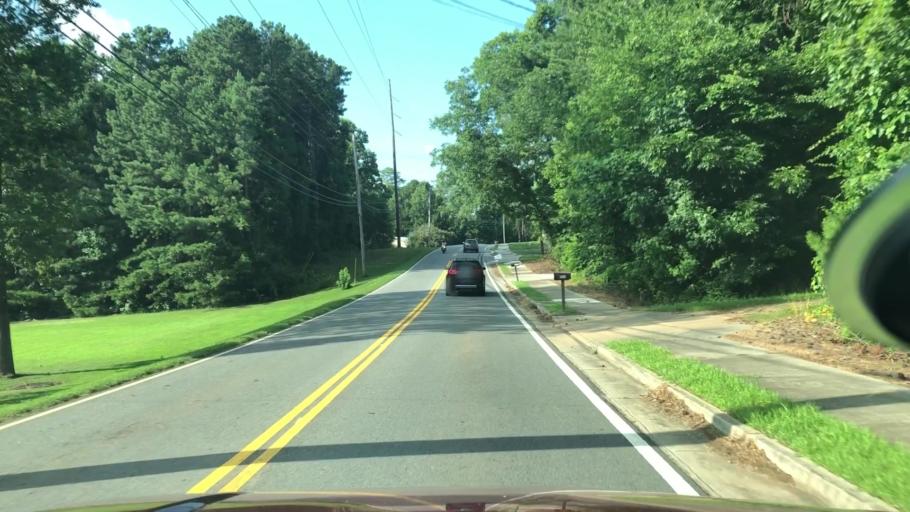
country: US
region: Georgia
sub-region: Cobb County
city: Acworth
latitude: 34.0953
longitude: -84.6136
